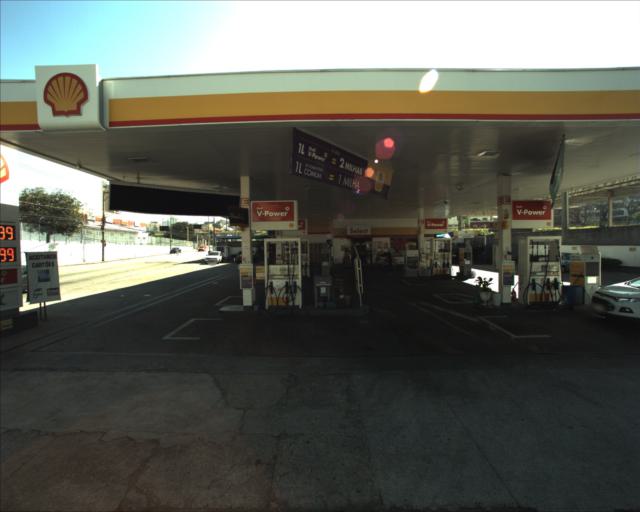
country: BR
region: Sao Paulo
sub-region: Sorocaba
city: Sorocaba
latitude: -23.4965
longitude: -47.4659
